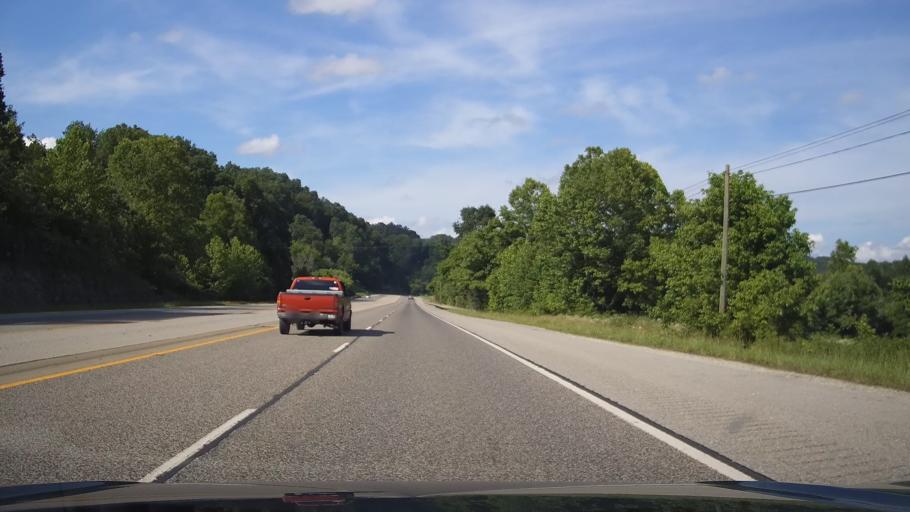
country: US
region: Kentucky
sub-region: Lawrence County
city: Louisa
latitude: 38.0132
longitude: -82.6610
